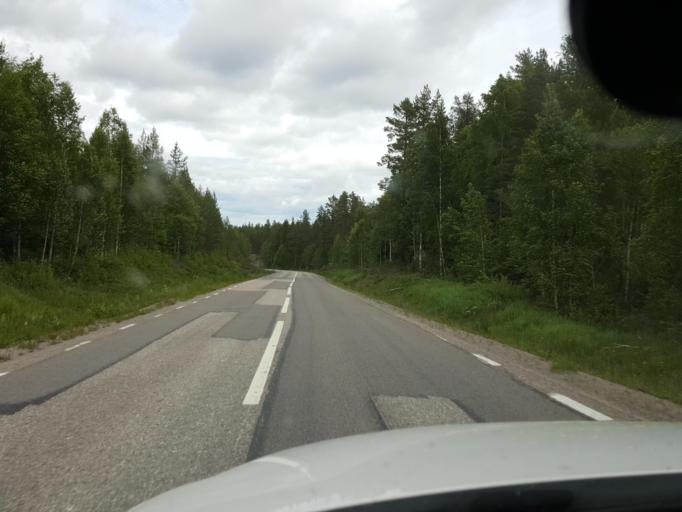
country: SE
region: Gaevleborg
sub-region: Ljusdals Kommun
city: Farila
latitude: 61.7768
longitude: 15.5929
